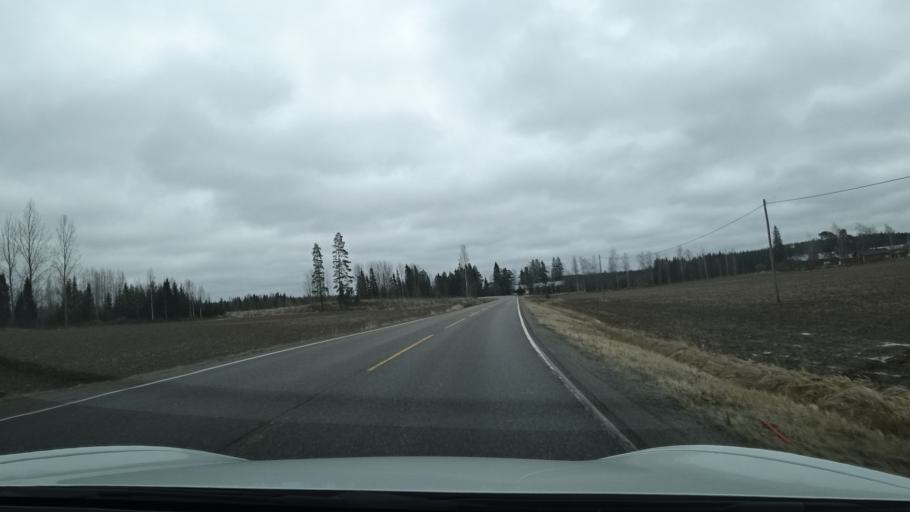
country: FI
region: Uusimaa
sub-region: Helsinki
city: Pornainen
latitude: 60.4869
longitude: 25.4485
